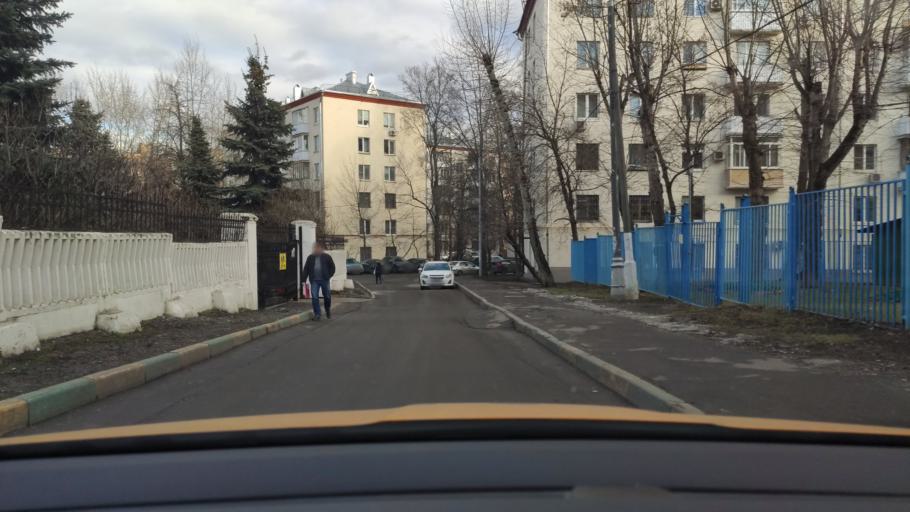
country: RU
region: Moskovskaya
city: Kozhukhovo
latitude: 55.6788
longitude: 37.6589
